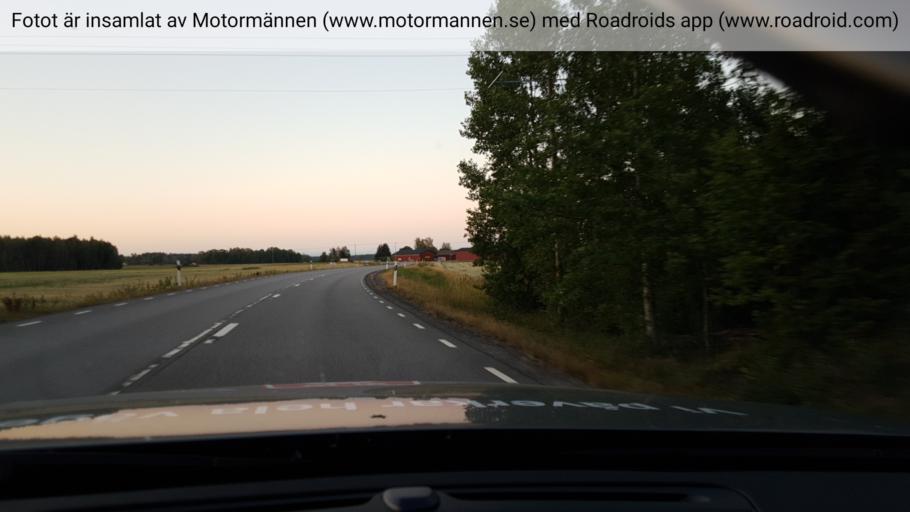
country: SE
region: Uppsala
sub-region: Heby Kommun
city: OEstervala
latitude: 60.1114
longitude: 17.2096
